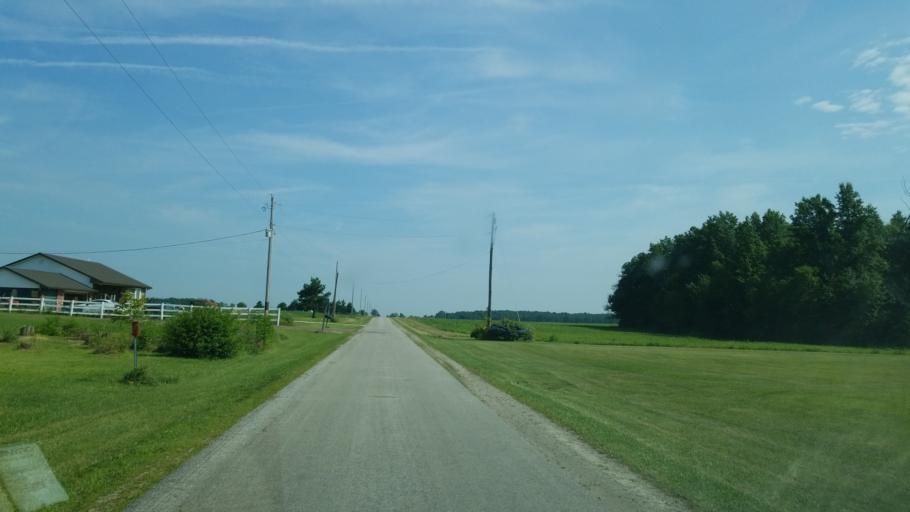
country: US
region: Ohio
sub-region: Sandusky County
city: Green Springs
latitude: 41.0893
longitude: -82.9960
